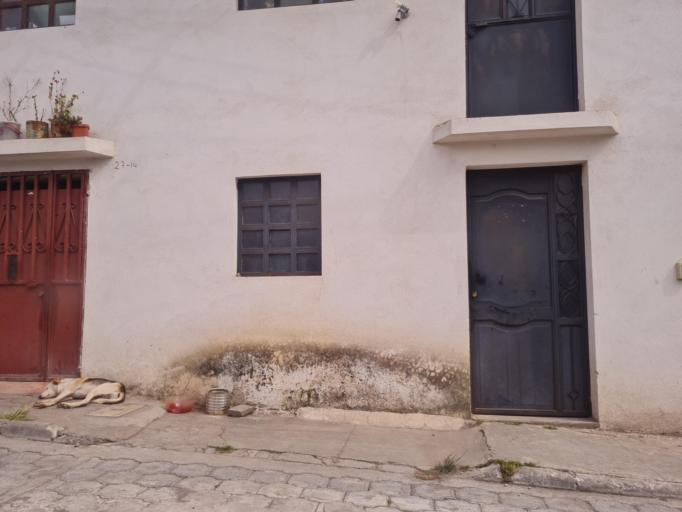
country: GT
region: Quetzaltenango
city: Quetzaltenango
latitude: 14.8362
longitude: -91.5323
